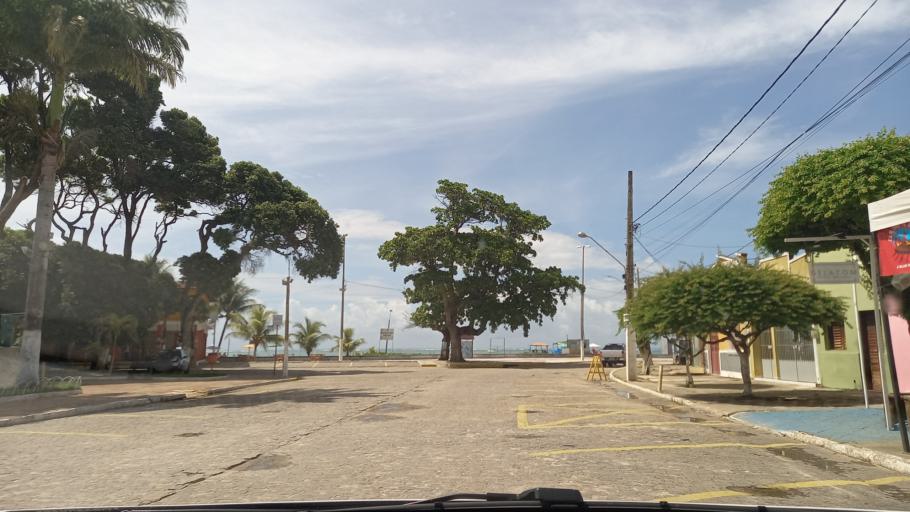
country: BR
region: Pernambuco
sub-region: Sao Jose Da Coroa Grande
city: Sao Jose da Coroa Grande
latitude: -8.8991
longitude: -35.1454
